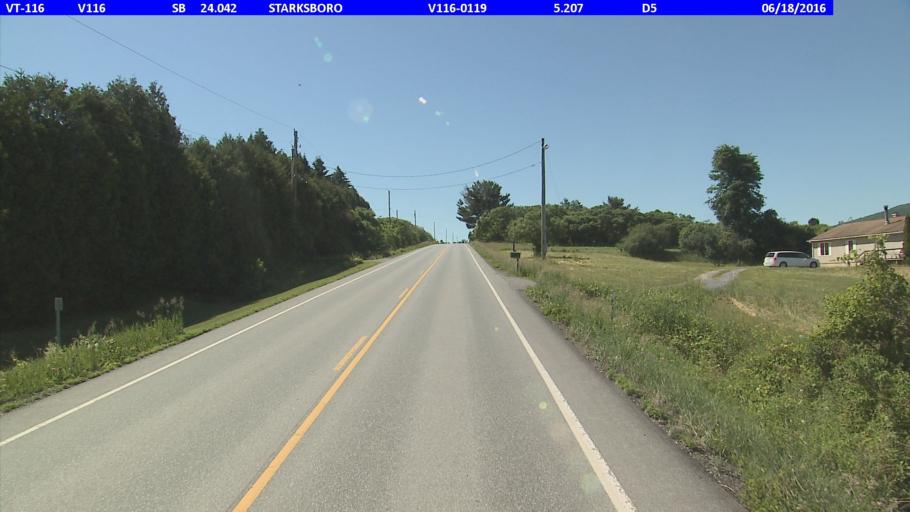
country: US
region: Vermont
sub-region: Chittenden County
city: Hinesburg
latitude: 44.2593
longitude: -73.0642
